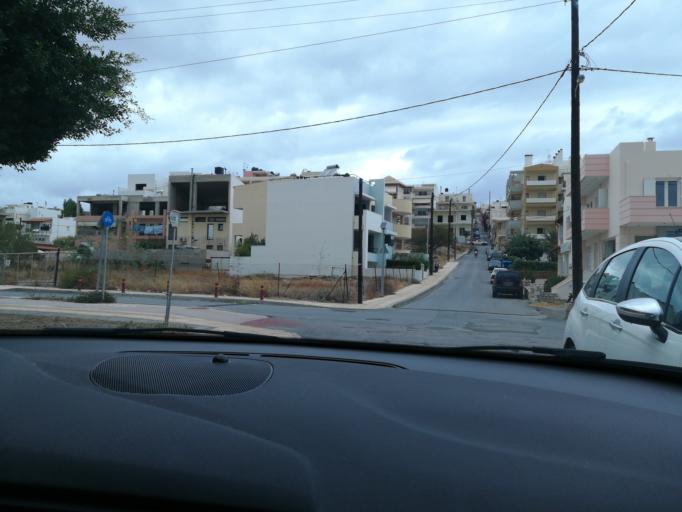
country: GR
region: Crete
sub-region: Nomos Lasithiou
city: Siteia
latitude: 35.2052
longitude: 26.1009
